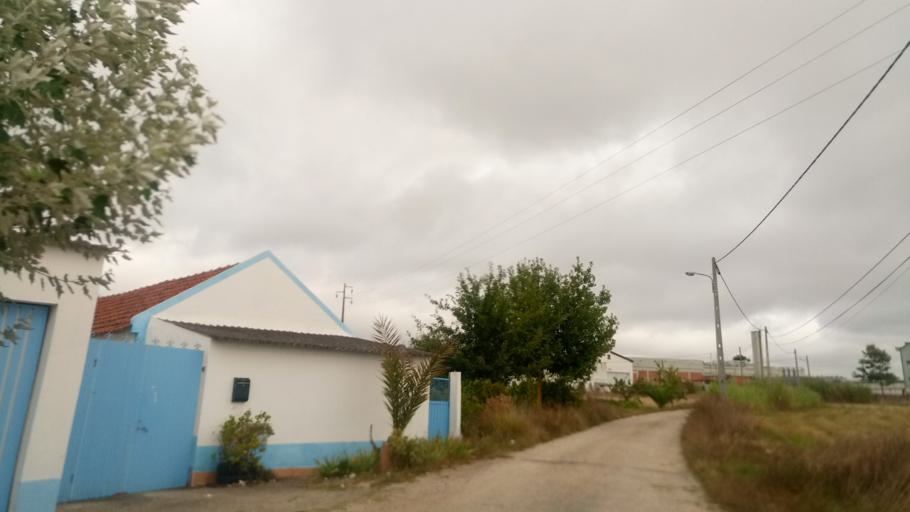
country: PT
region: Leiria
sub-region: Caldas da Rainha
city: Caldas da Rainha
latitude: 39.4284
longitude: -9.1346
